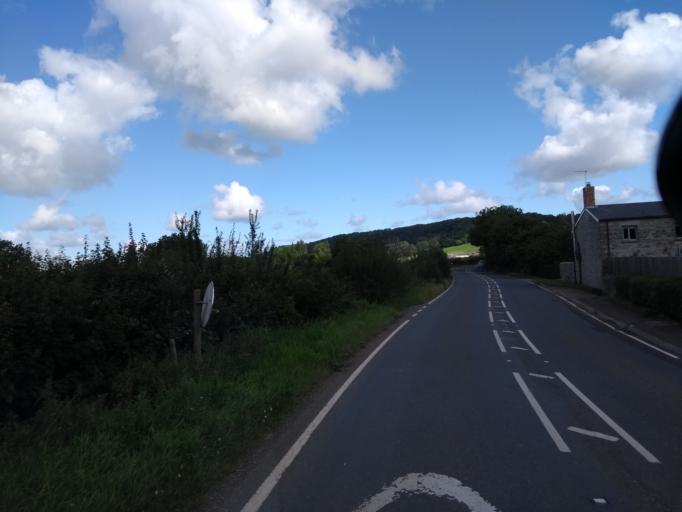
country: GB
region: England
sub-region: Somerset
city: Street
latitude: 51.0983
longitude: -2.7353
